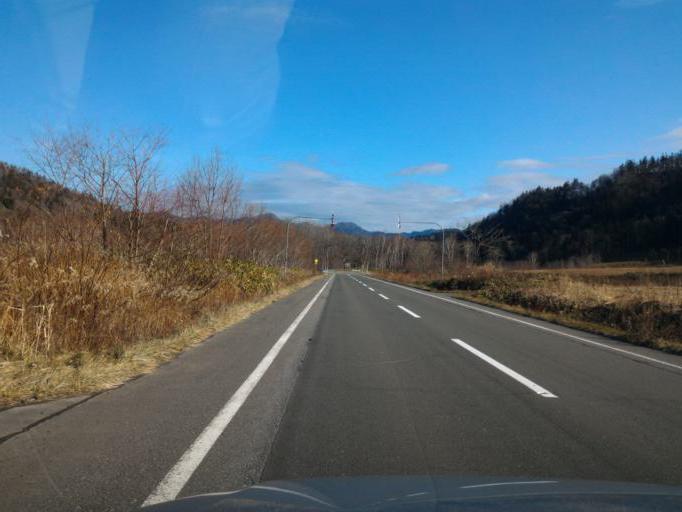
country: JP
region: Hokkaido
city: Ashibetsu
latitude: 43.3071
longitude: 142.1225
